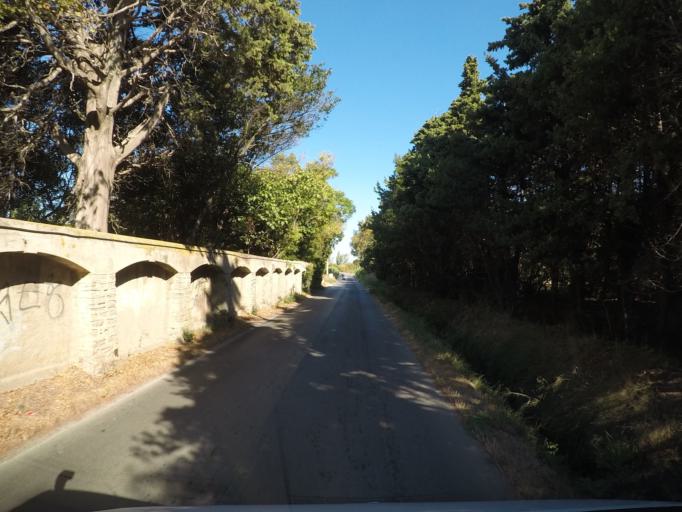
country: FR
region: Languedoc-Roussillon
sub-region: Departement de l'Aude
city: Narbonne
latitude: 43.1699
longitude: 3.0090
